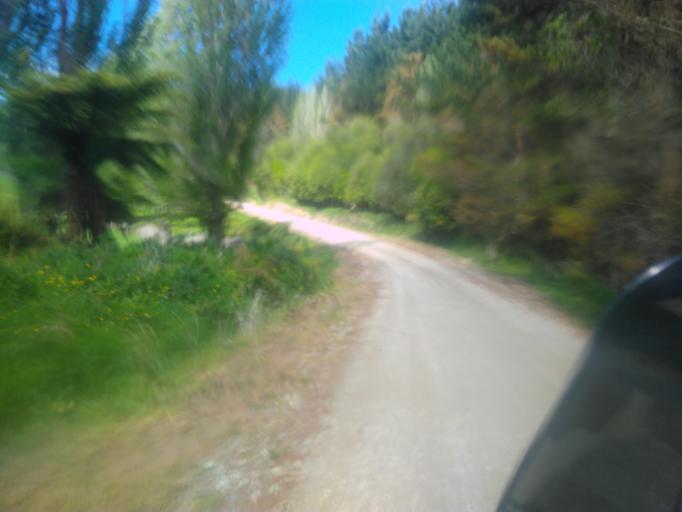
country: NZ
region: Hawke's Bay
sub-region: Wairoa District
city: Wairoa
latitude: -38.7712
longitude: 177.5984
